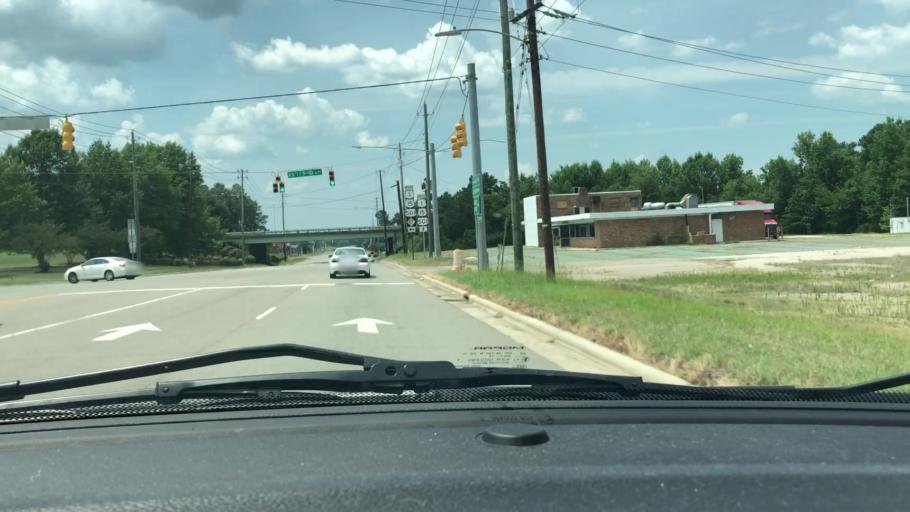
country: US
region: North Carolina
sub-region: Lee County
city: Sanford
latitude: 35.4941
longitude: -79.1935
